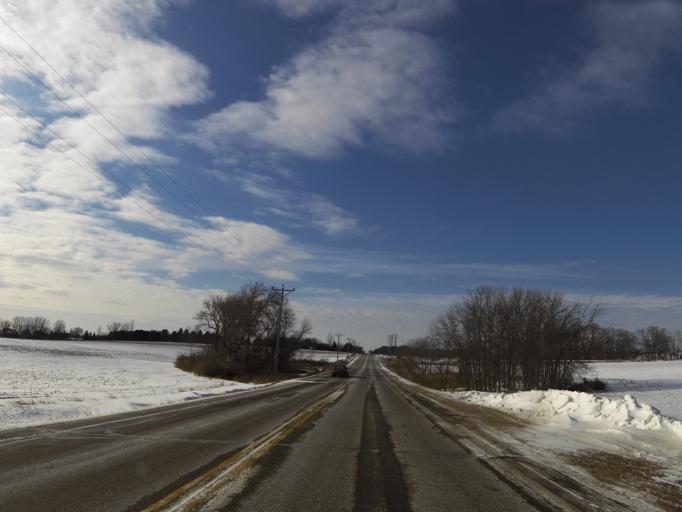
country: US
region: Wisconsin
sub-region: Saint Croix County
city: Roberts
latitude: 44.9928
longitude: -92.5732
